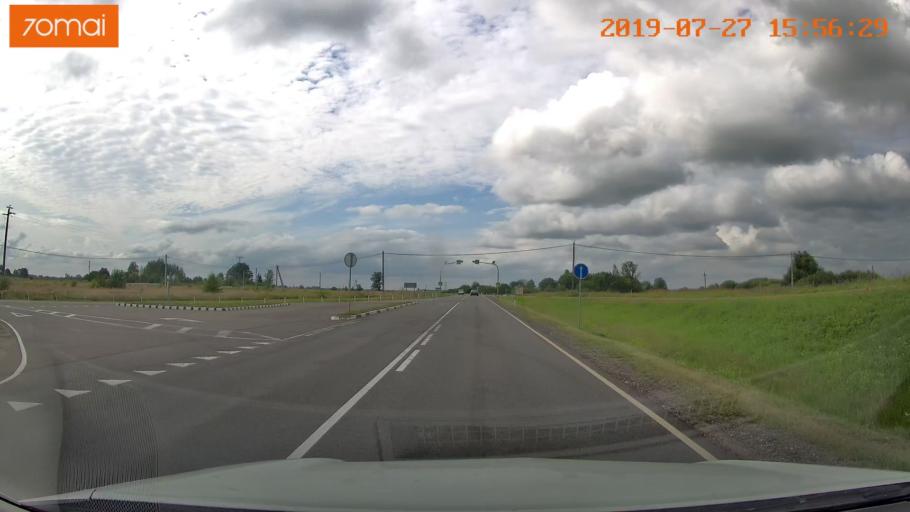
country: RU
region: Kaliningrad
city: Chernyakhovsk
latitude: 54.6195
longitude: 21.9010
